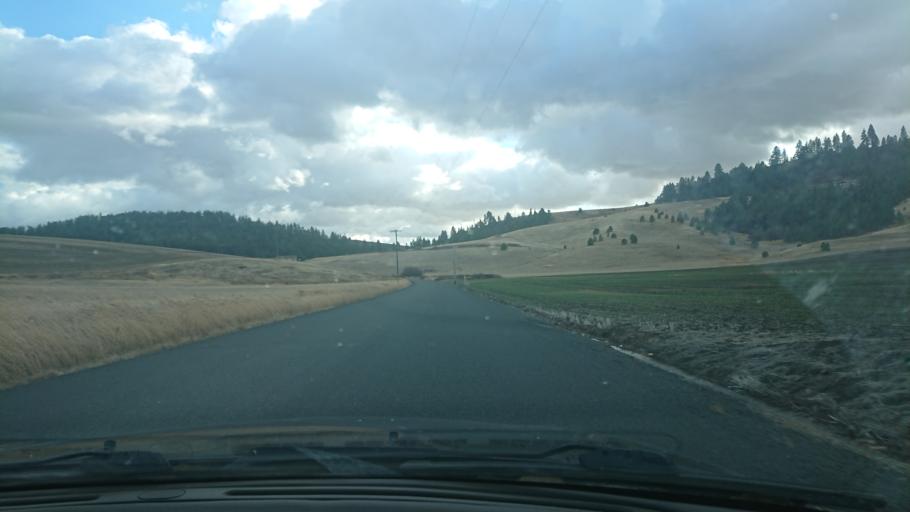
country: US
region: Idaho
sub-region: Latah County
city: Moscow
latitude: 46.7071
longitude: -116.8650
